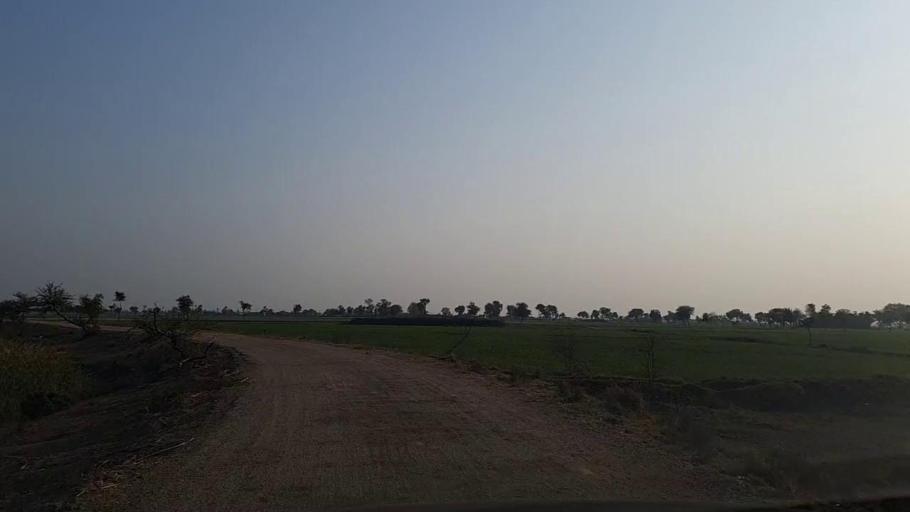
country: PK
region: Sindh
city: Daur
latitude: 26.4015
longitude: 68.3882
